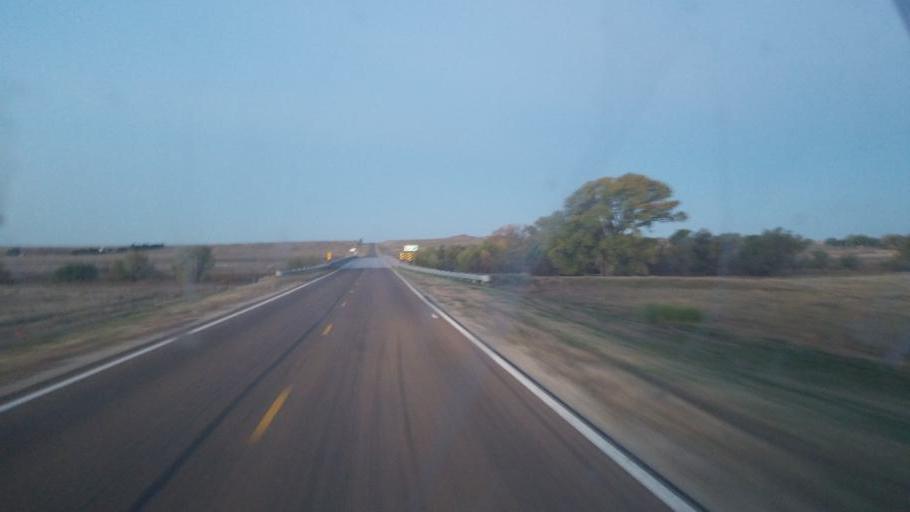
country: US
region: Kansas
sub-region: Wallace County
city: Sharon Springs
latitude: 39.0185
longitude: -101.3464
